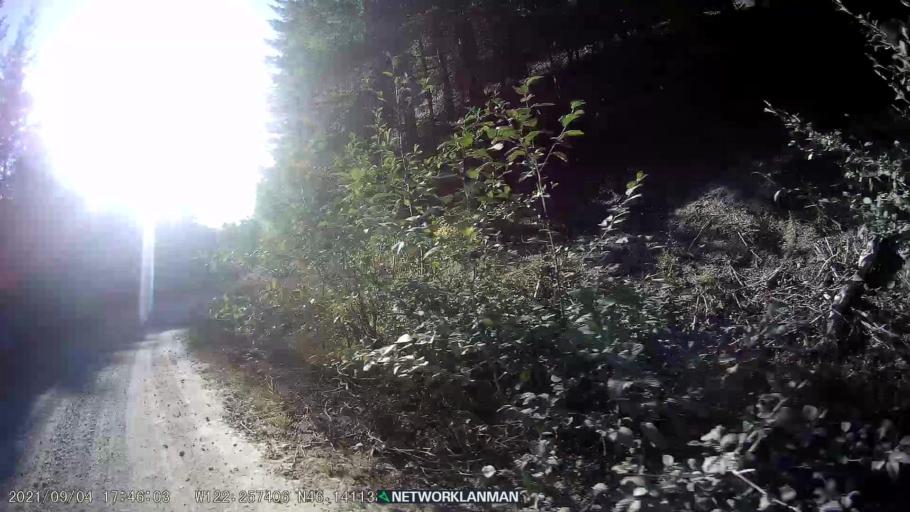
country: US
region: Washington
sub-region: Clark County
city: Amboy
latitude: 46.1411
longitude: -122.2575
